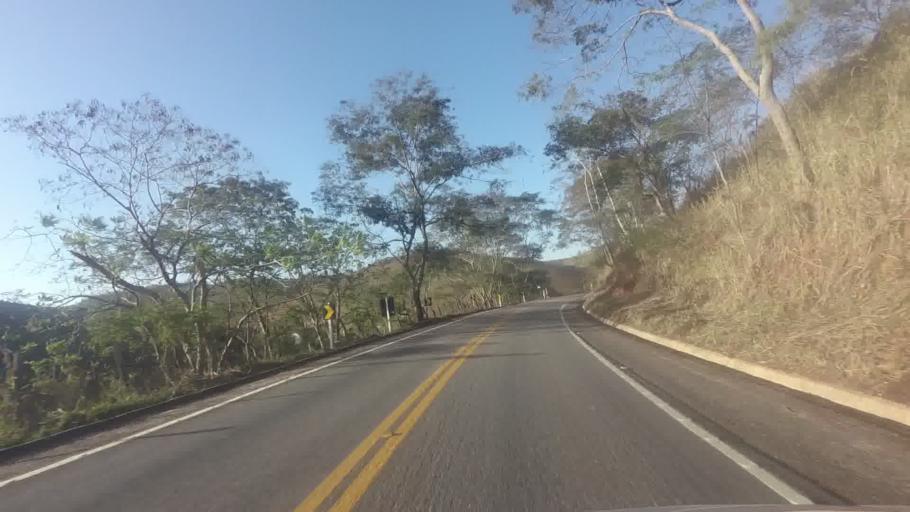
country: BR
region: Espirito Santo
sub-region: Jeronimo Monteiro
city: Jeronimo Monteiro
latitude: -20.8878
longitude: -41.2798
